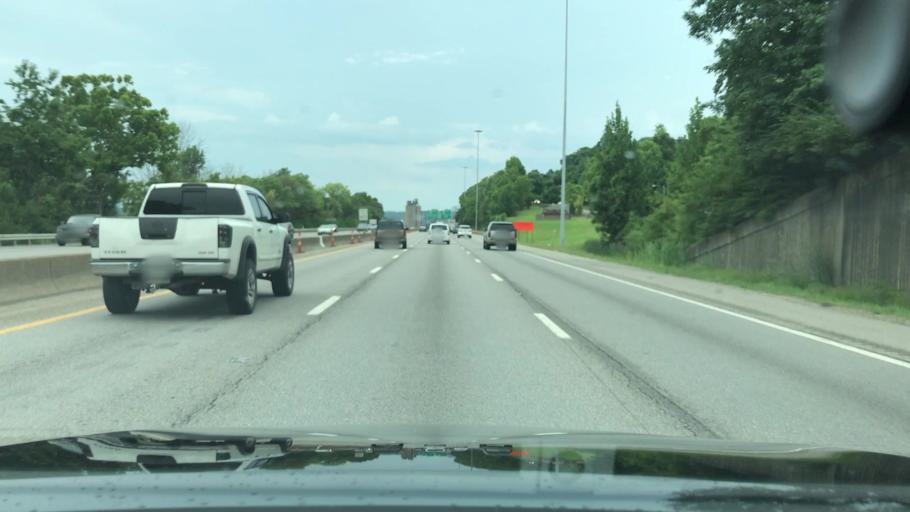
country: US
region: West Virginia
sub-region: Kanawha County
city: South Charleston
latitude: 38.3633
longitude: -81.6742
